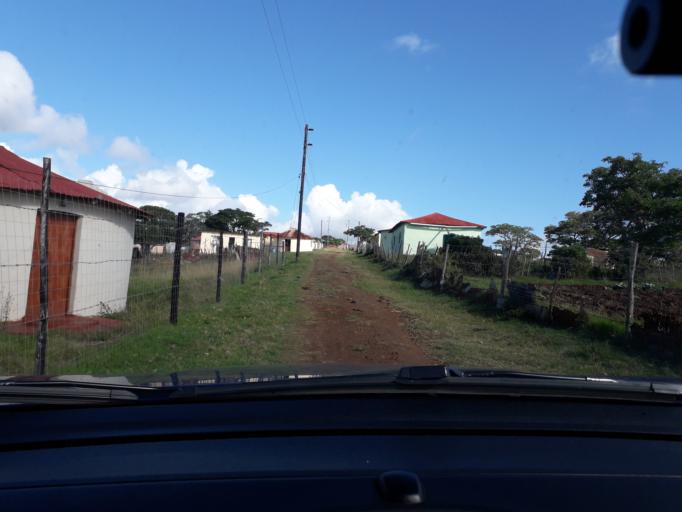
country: ZA
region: Eastern Cape
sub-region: Buffalo City Metropolitan Municipality
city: Bhisho
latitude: -33.1092
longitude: 27.4298
